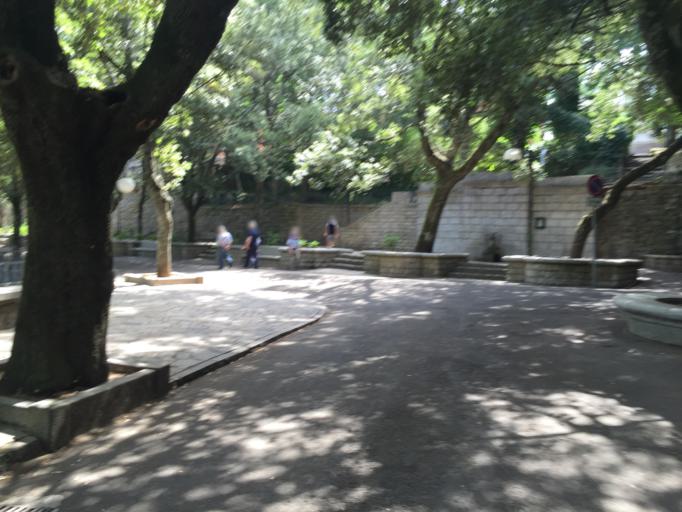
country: IT
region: Sardinia
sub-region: Provincia di Olbia-Tempio
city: Tempio Pausania
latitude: 40.8995
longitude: 9.0993
